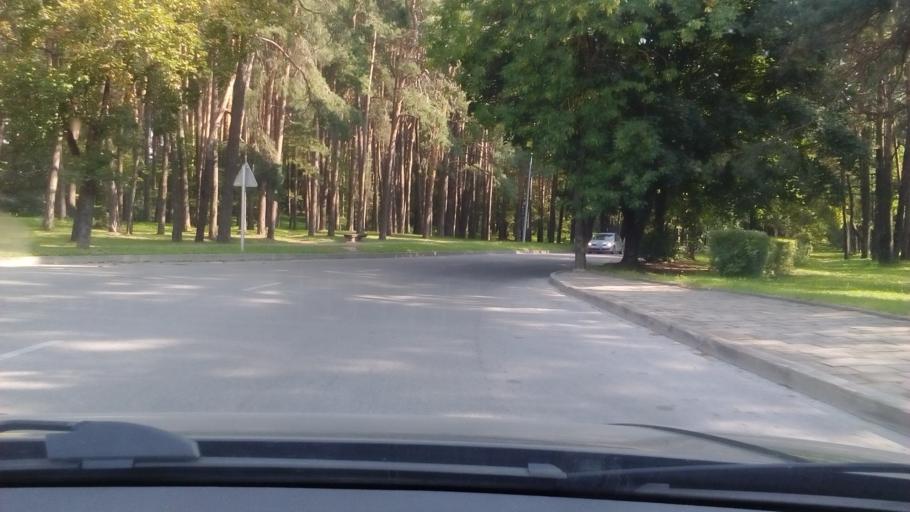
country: LT
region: Alytaus apskritis
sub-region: Alytus
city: Alytus
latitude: 54.3964
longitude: 24.0509
